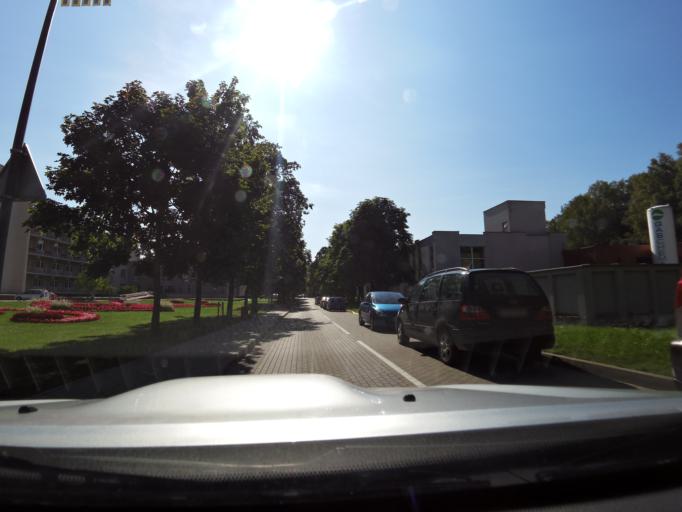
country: LT
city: Birstonas
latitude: 54.6011
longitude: 24.0294
